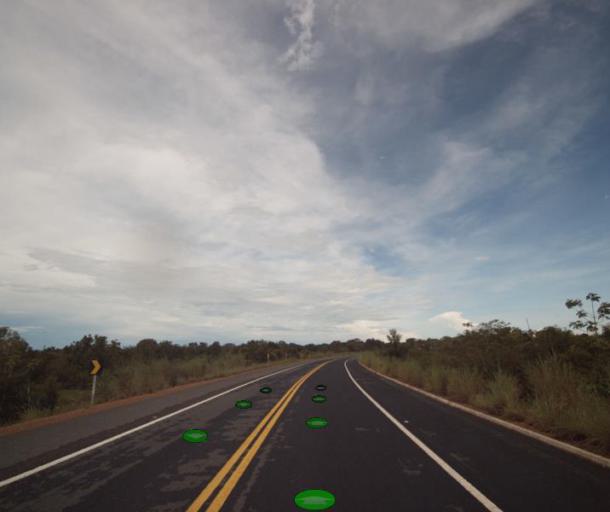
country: BR
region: Goias
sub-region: Sao Miguel Do Araguaia
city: Sao Miguel do Araguaia
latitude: -13.2400
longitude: -50.5423
